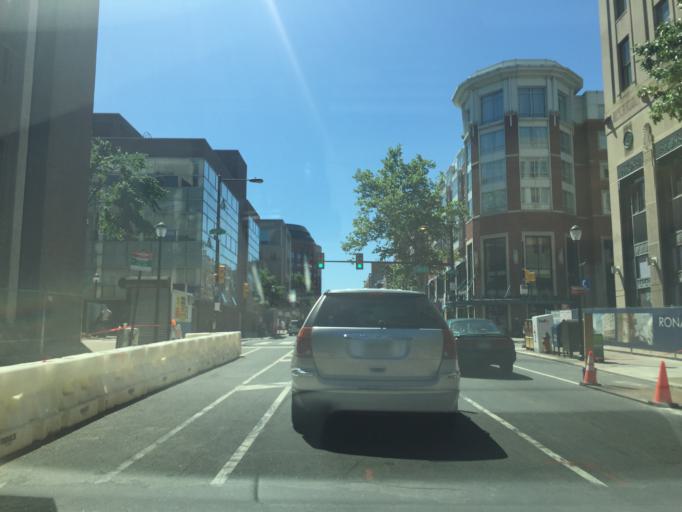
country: US
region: Pennsylvania
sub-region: Philadelphia County
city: Philadelphia
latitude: 39.9531
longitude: -75.1944
